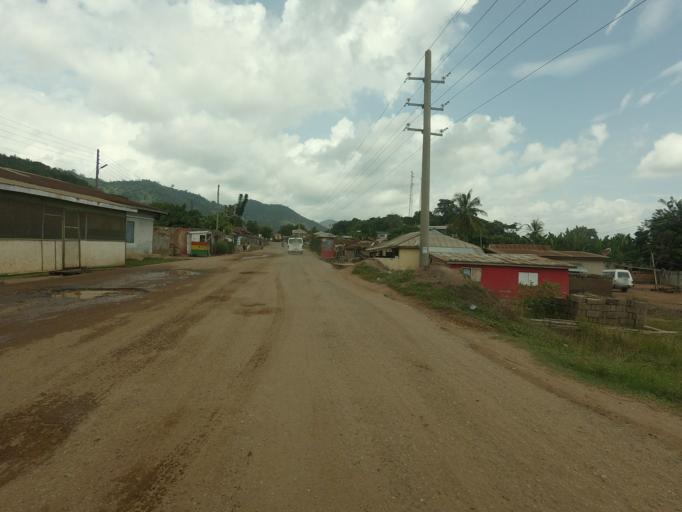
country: GH
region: Volta
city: Ho
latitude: 6.6897
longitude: 0.3337
